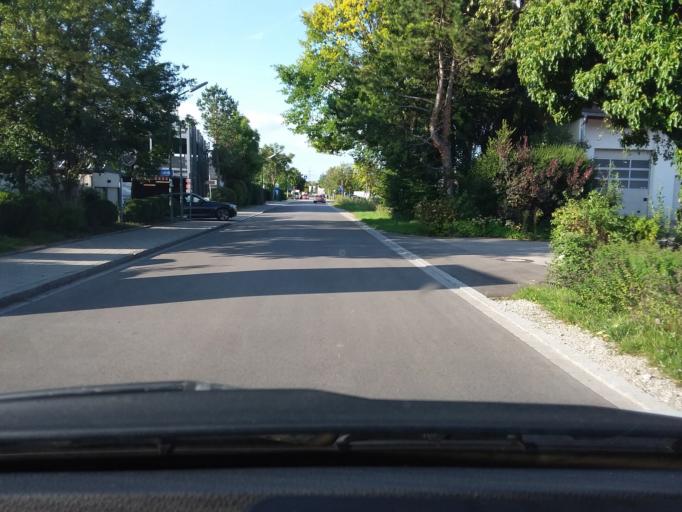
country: DE
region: Bavaria
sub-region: Upper Bavaria
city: Ismaning
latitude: 48.2294
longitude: 11.6866
